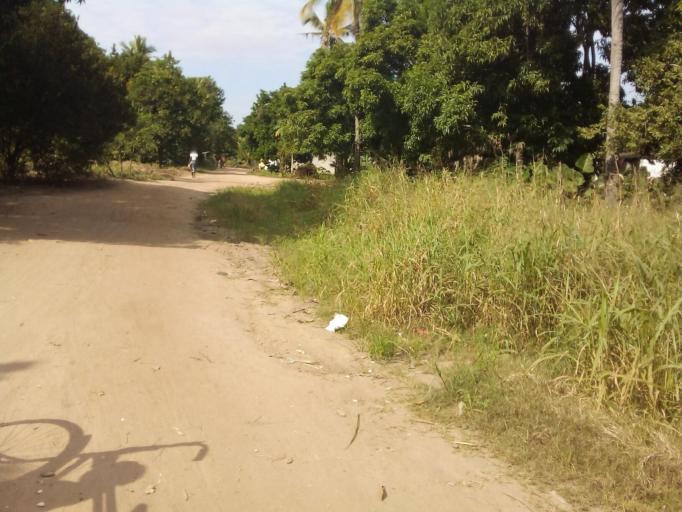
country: MZ
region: Zambezia
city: Quelimane
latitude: -17.5802
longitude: 36.6957
